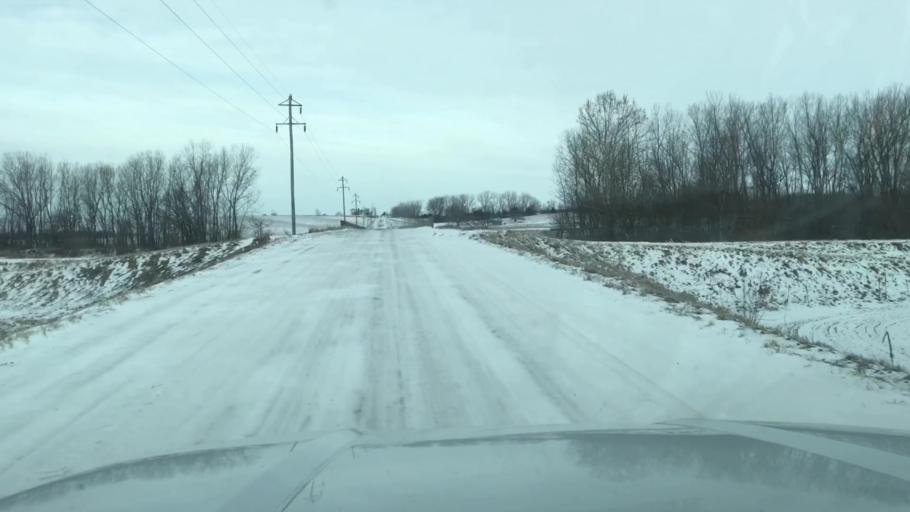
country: US
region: Missouri
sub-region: Holt County
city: Oregon
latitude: 40.1301
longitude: -95.0499
